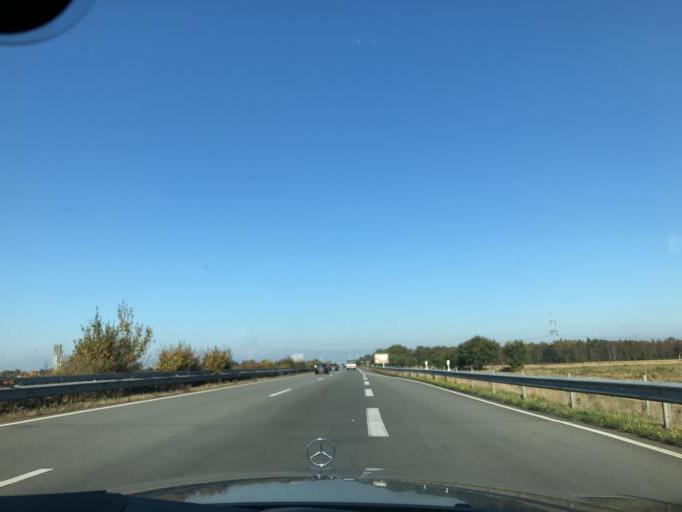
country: DE
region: Lower Saxony
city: Bunde
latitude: 53.1411
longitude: 7.2750
